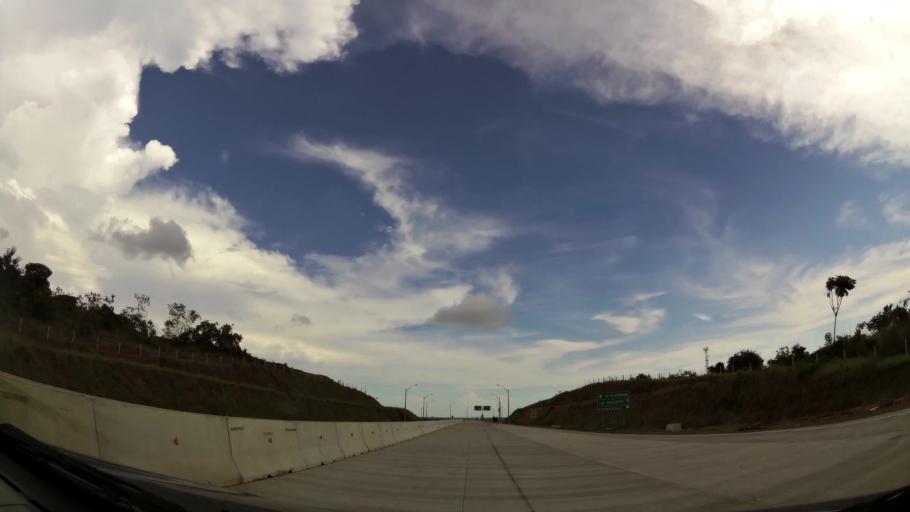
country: PA
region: Panama
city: Tocumen
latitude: 9.1013
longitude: -79.3928
